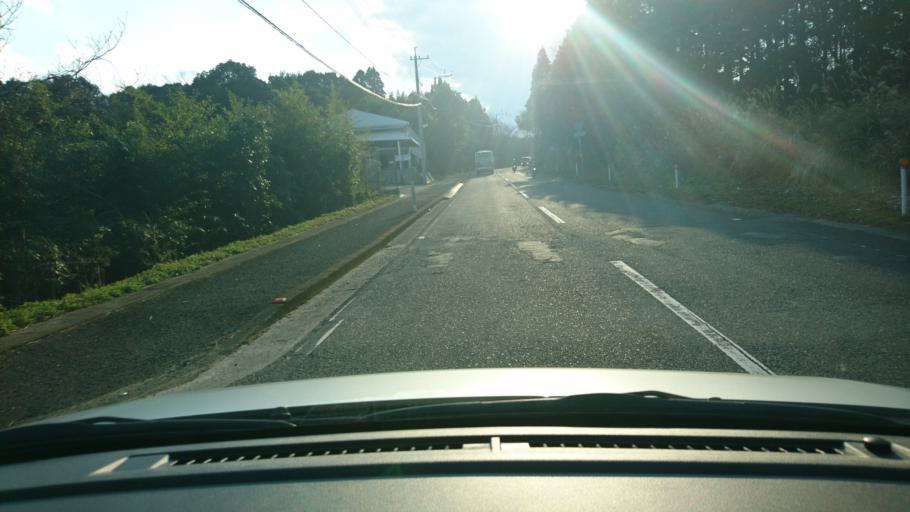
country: JP
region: Miyazaki
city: Miyazaki-shi
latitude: 31.8647
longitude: 131.4034
